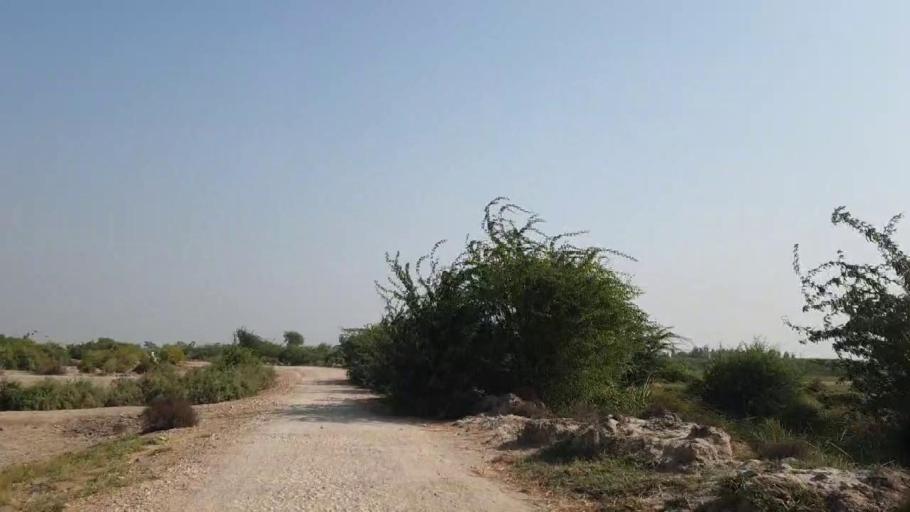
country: PK
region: Sindh
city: Bulri
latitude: 24.9308
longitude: 68.3758
